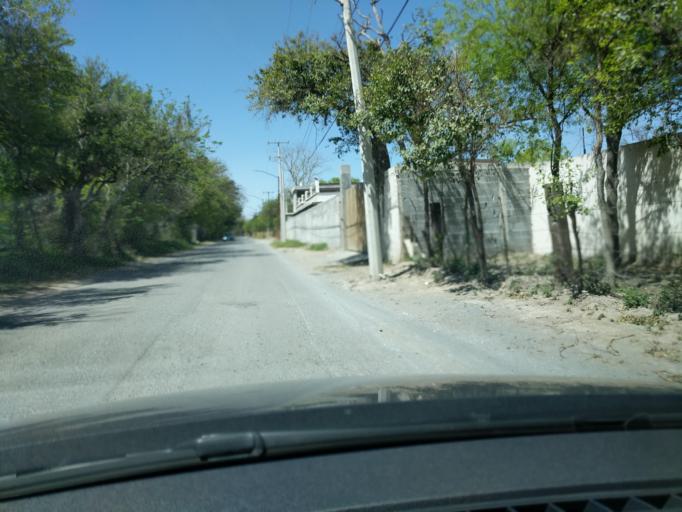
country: MX
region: Nuevo Leon
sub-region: Pesqueria
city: Colinas del Aeropuerto
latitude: 25.8118
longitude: -100.1281
